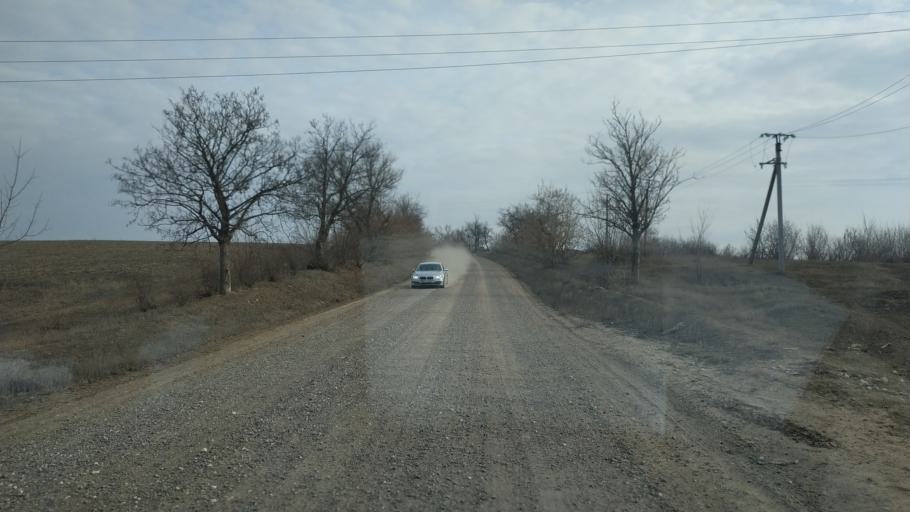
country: MD
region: Chisinau
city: Vadul lui Voda
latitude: 46.9754
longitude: 29.0760
